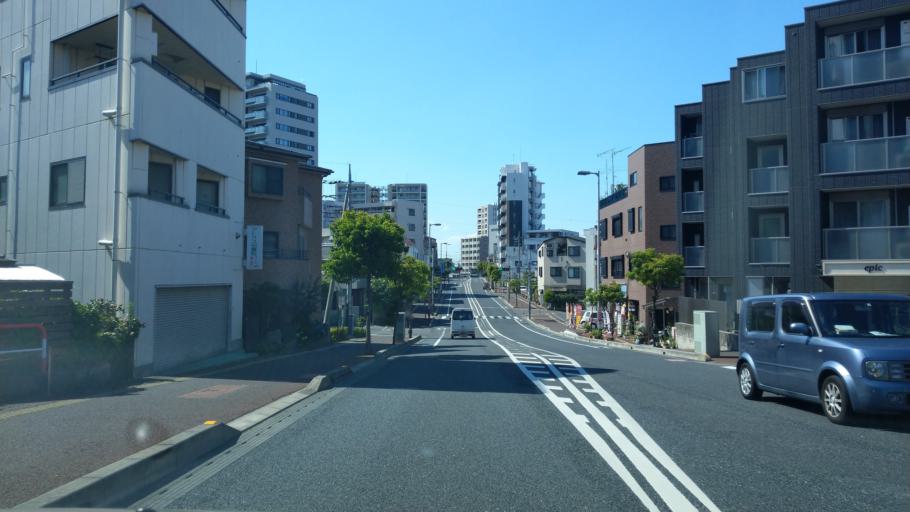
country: JP
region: Saitama
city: Yono
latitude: 35.8600
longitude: 139.6590
